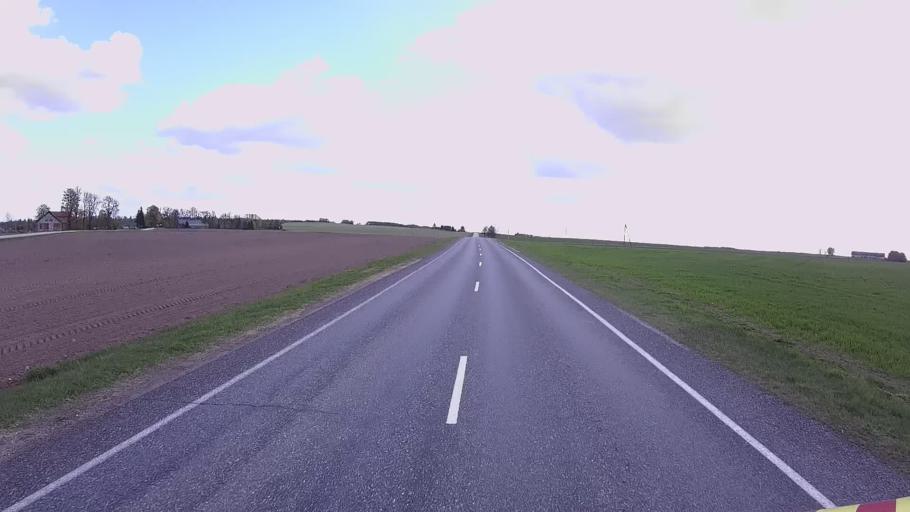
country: EE
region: Jogevamaa
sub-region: Jogeva linn
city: Jogeva
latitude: 58.7980
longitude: 26.4860
